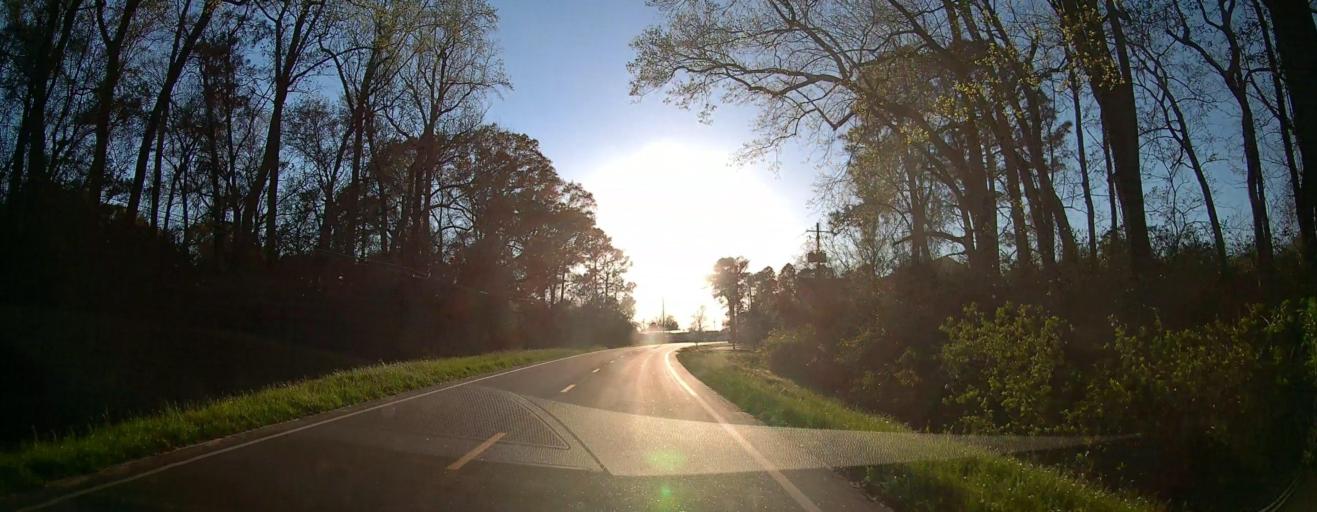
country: US
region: Georgia
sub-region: Wilcox County
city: Rochelle
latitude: 31.9451
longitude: -83.5362
